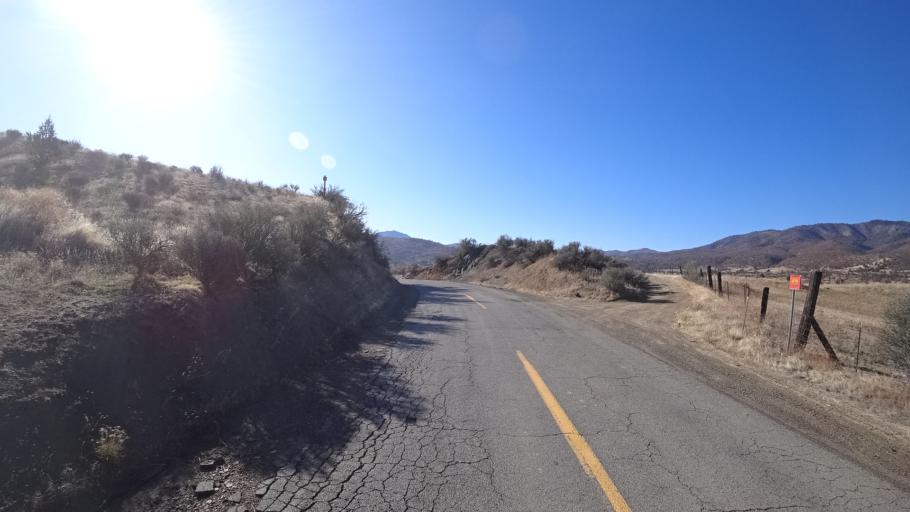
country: US
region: California
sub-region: Siskiyou County
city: Montague
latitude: 41.9005
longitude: -122.5443
